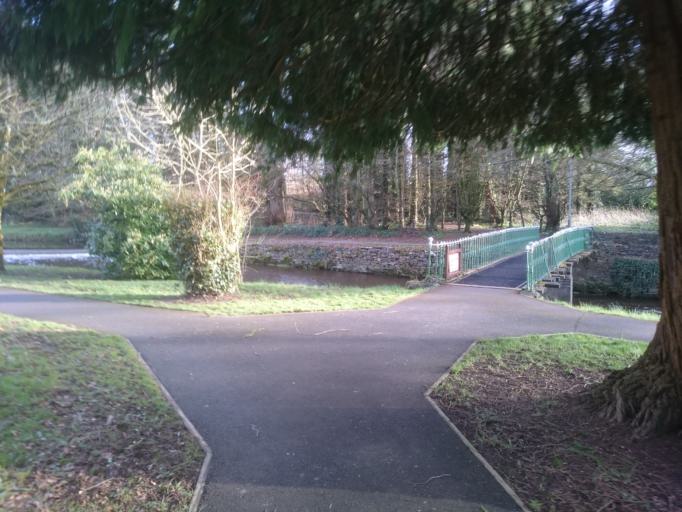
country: IE
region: Connaught
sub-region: Roscommon
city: Castlerea
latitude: 53.7693
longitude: -8.4885
